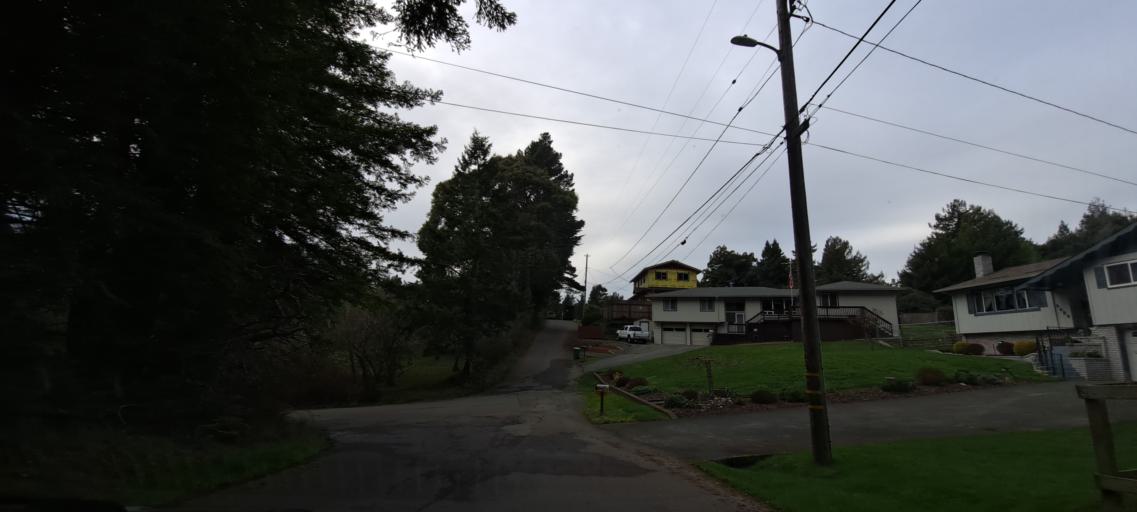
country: US
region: California
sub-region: Humboldt County
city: Fortuna
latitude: 40.6062
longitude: -124.1546
